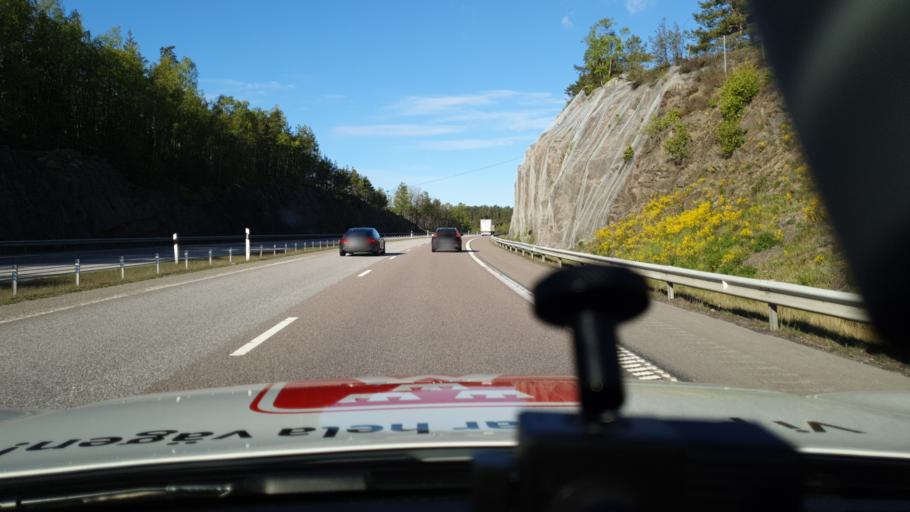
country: SE
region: OEstergoetland
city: Lindo
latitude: 58.6719
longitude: 16.2473
